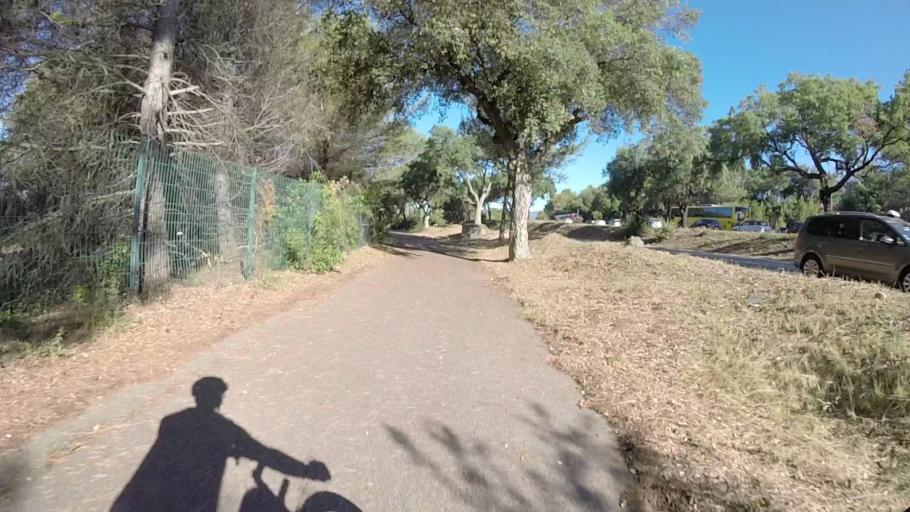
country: FR
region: Provence-Alpes-Cote d'Azur
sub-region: Departement des Alpes-Maritimes
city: Biot
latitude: 43.6158
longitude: 7.0775
